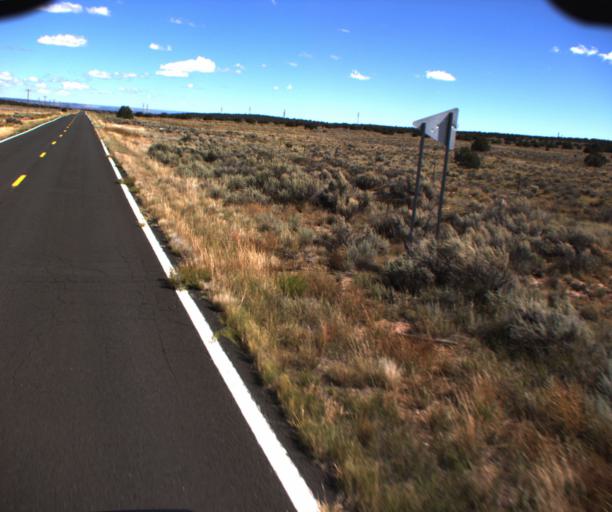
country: US
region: New Mexico
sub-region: McKinley County
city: Zuni Pueblo
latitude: 35.0109
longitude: -109.0682
